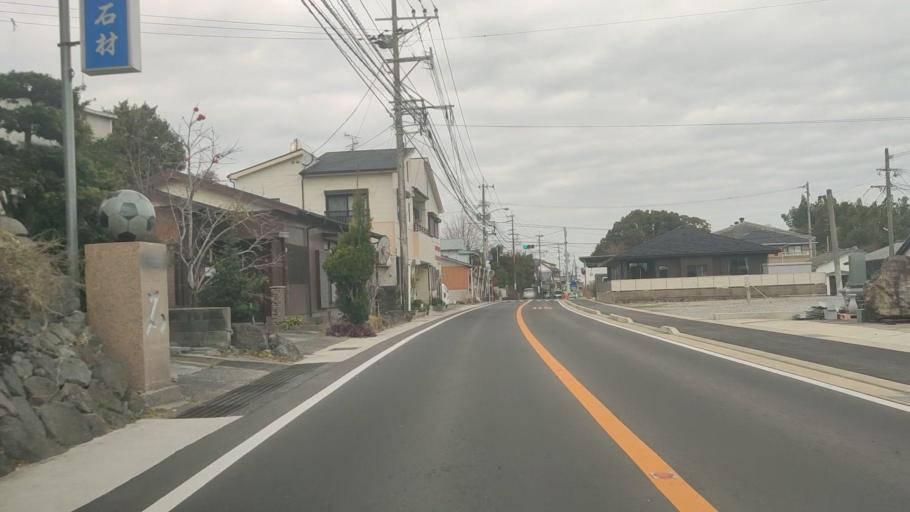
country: JP
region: Nagasaki
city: Shimabara
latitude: 32.8169
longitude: 130.3553
